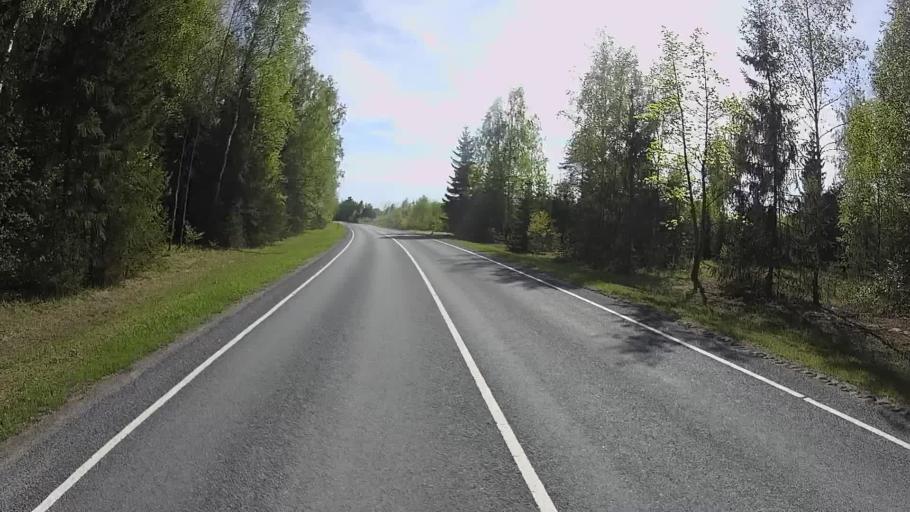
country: EE
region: Vorumaa
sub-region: Antsla vald
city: Vana-Antsla
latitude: 57.9645
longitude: 26.4570
